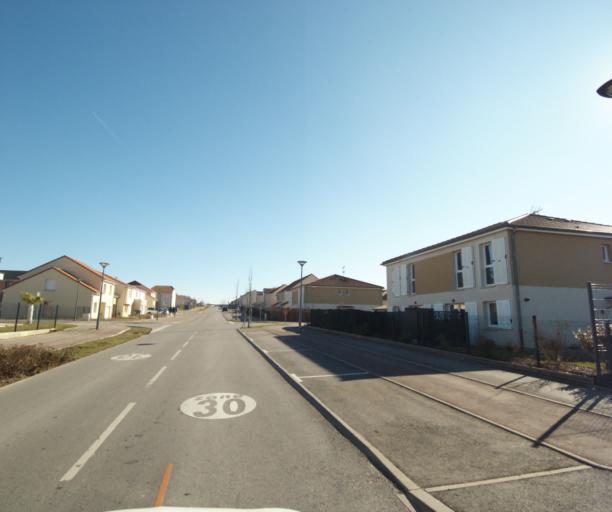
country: FR
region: Lorraine
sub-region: Departement de Meurthe-et-Moselle
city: Tomblaine
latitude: 48.6799
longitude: 6.2265
